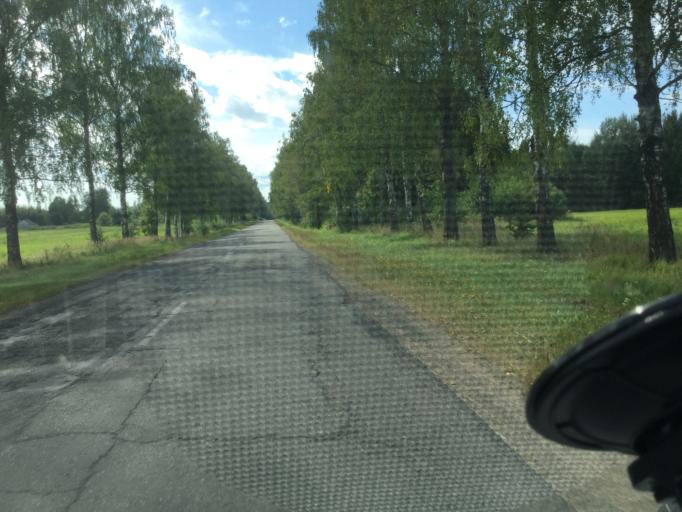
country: BY
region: Vitebsk
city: Chashniki
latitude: 55.3059
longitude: 29.3990
